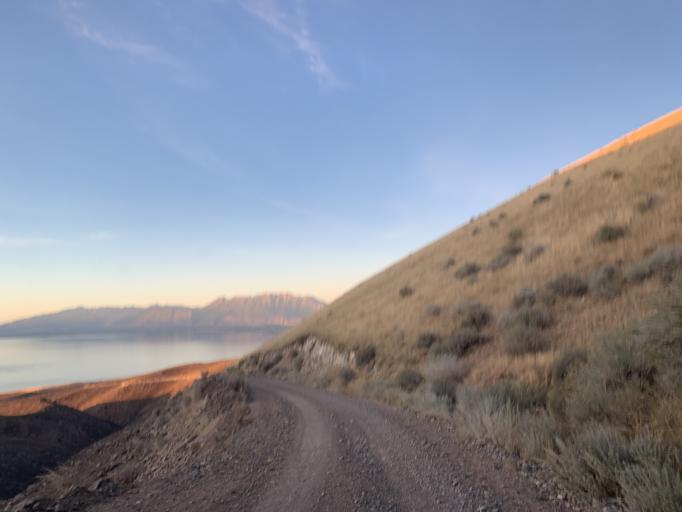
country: US
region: Utah
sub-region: Utah County
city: West Mountain
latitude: 40.1004
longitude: -111.8240
